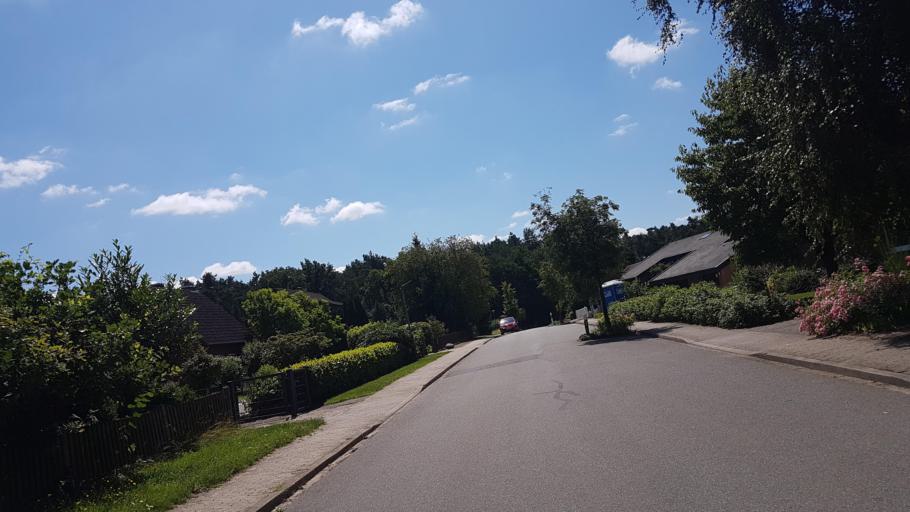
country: DE
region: Lower Saxony
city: Rullstorf
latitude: 53.2834
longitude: 10.5306
